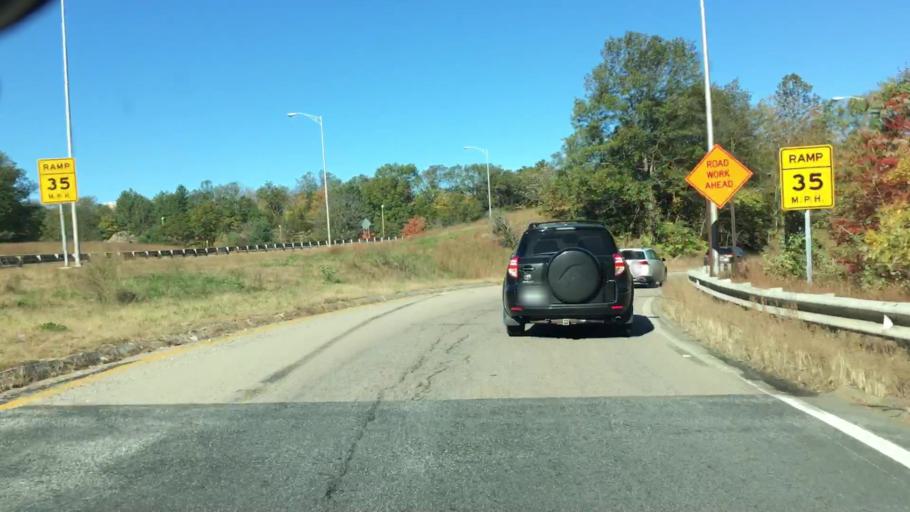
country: US
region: Massachusetts
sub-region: Middlesex County
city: Ashland
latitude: 42.2932
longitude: -71.4810
